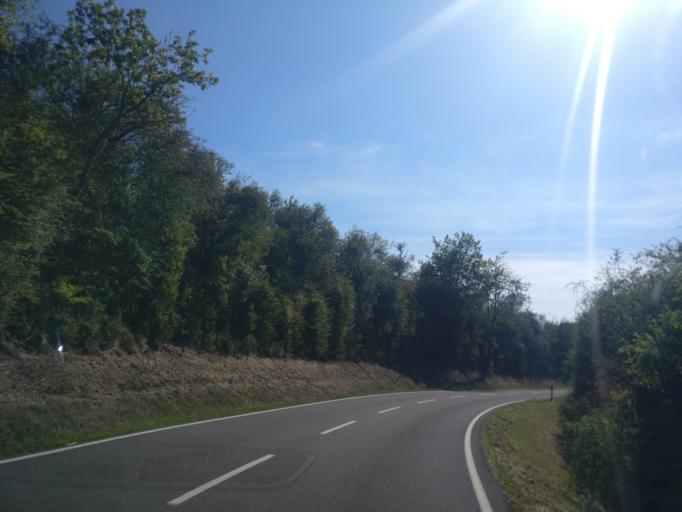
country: LU
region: Grevenmacher
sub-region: Canton de Grevenmacher
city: Wormeldange
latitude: 49.6437
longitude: 6.4016
